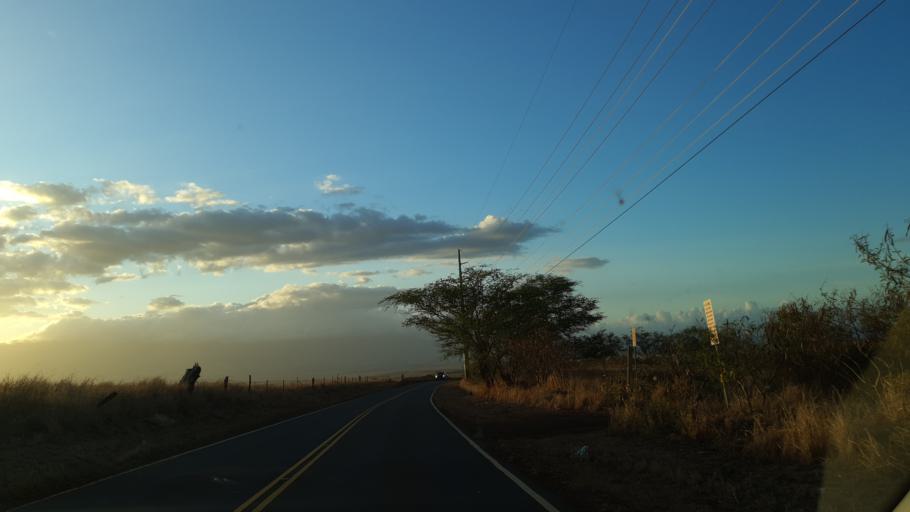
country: US
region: Hawaii
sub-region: Maui County
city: Pukalani
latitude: 20.7969
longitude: -156.3705
